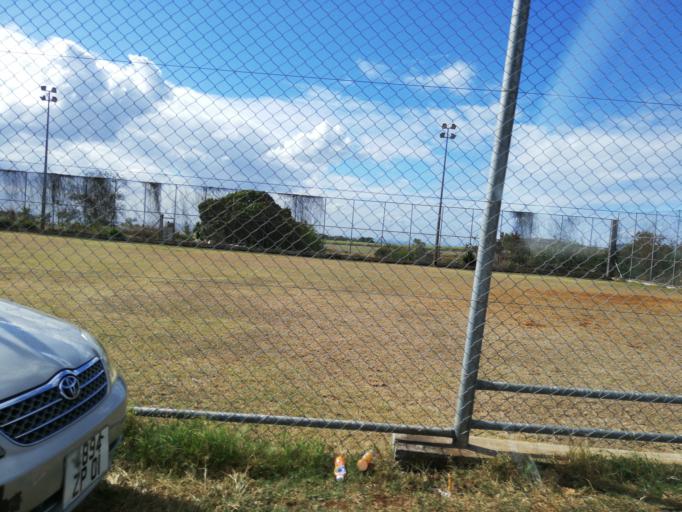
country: MU
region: Black River
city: Petite Riviere
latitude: -20.2226
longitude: 57.4551
